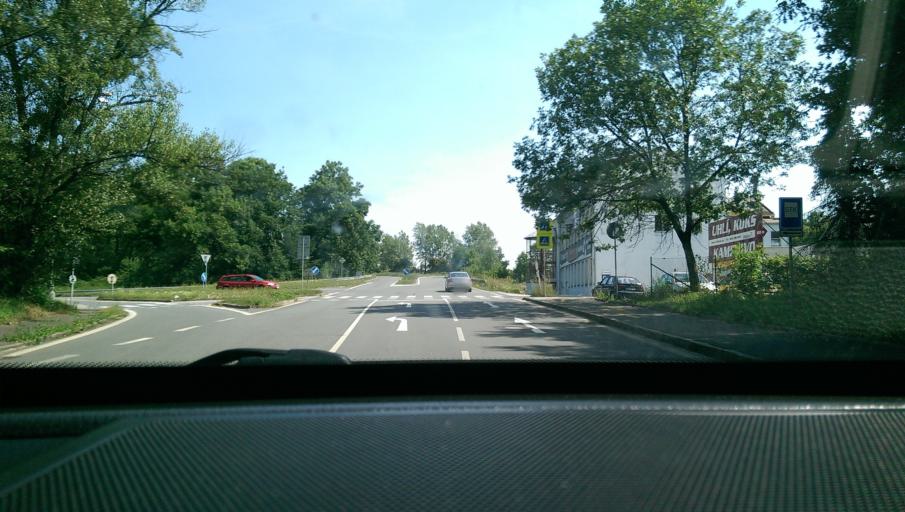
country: CZ
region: Moravskoslezsky
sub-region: Okres Ostrava-Mesto
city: Ostrava
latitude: 49.8368
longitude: 18.2418
